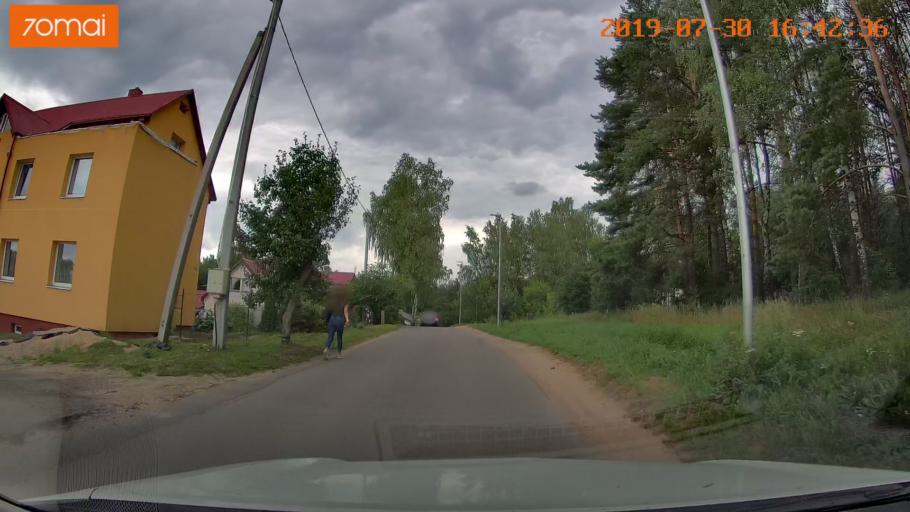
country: LT
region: Vilnius County
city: Rasos
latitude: 54.7167
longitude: 25.3529
